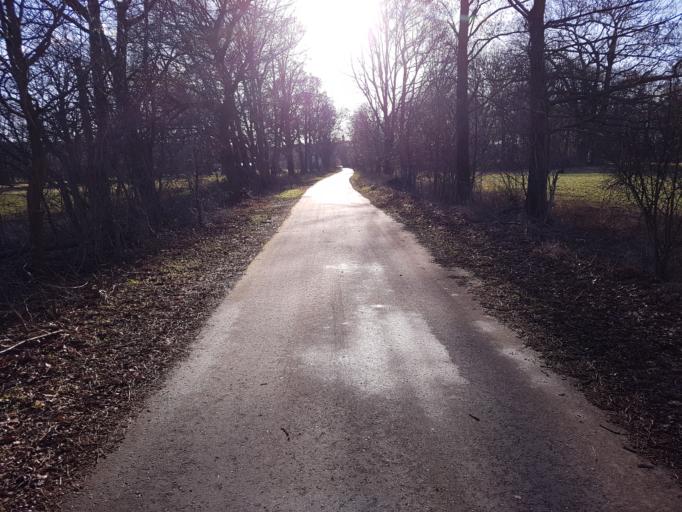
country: DE
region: Brandenburg
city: Groden
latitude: 51.4116
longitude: 13.5751
